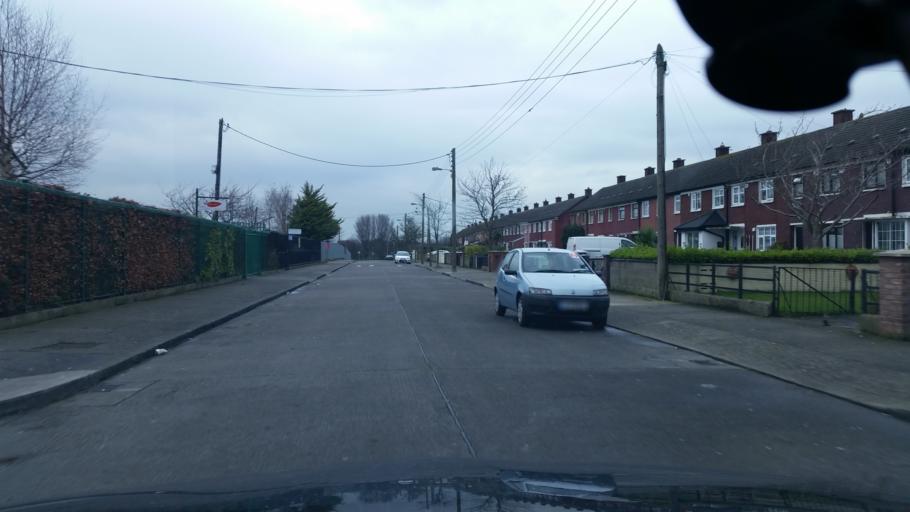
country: IE
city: Bonnybrook
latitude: 53.3939
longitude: -6.2058
